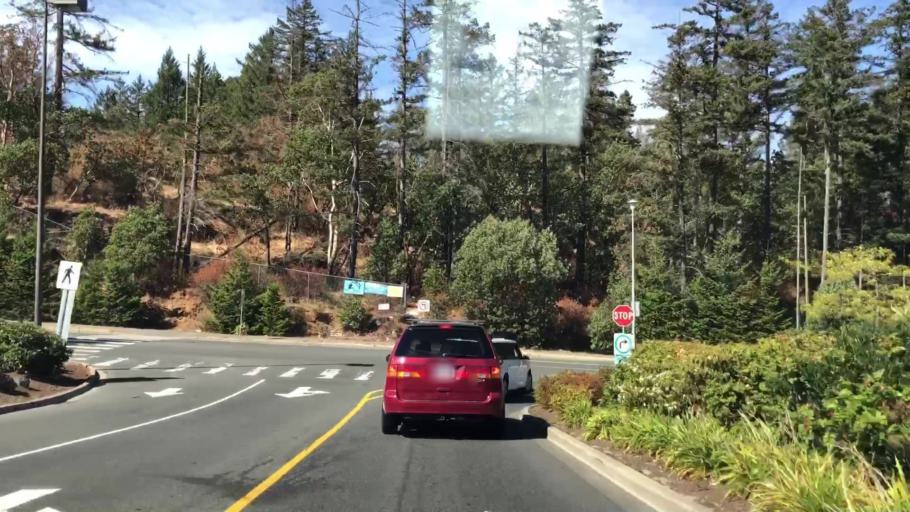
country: CA
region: British Columbia
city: Langford
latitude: 48.4591
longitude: -123.5014
